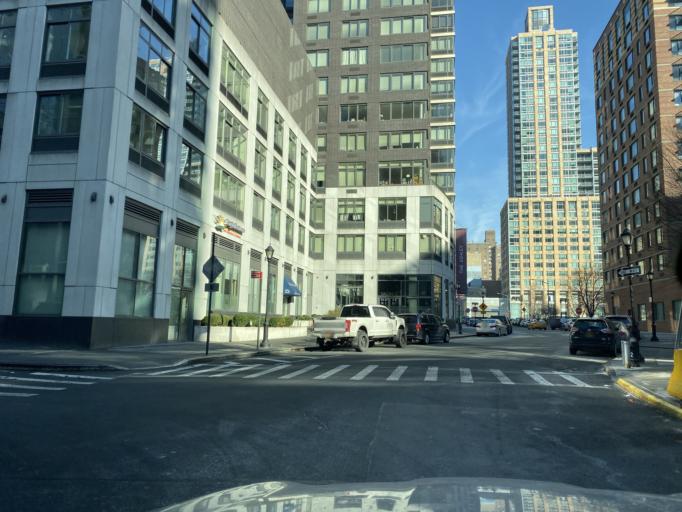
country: US
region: New Jersey
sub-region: Hudson County
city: Guttenberg
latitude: 40.7739
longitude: -73.9903
